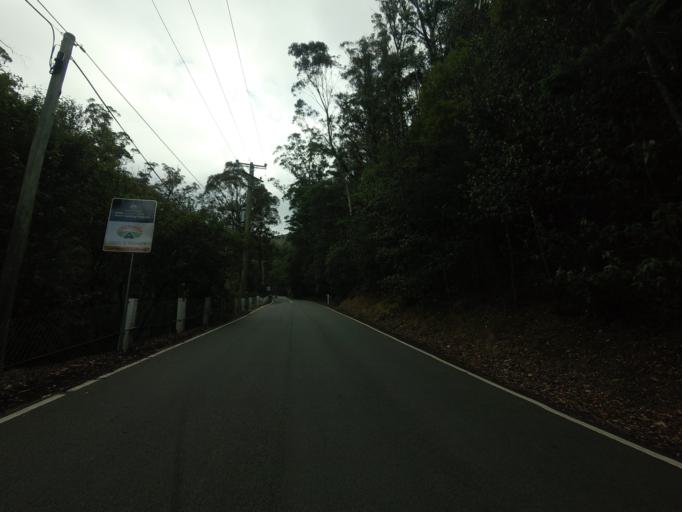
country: AU
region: Tasmania
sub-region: Hobart
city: Dynnyrne
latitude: -42.9072
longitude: 147.2655
